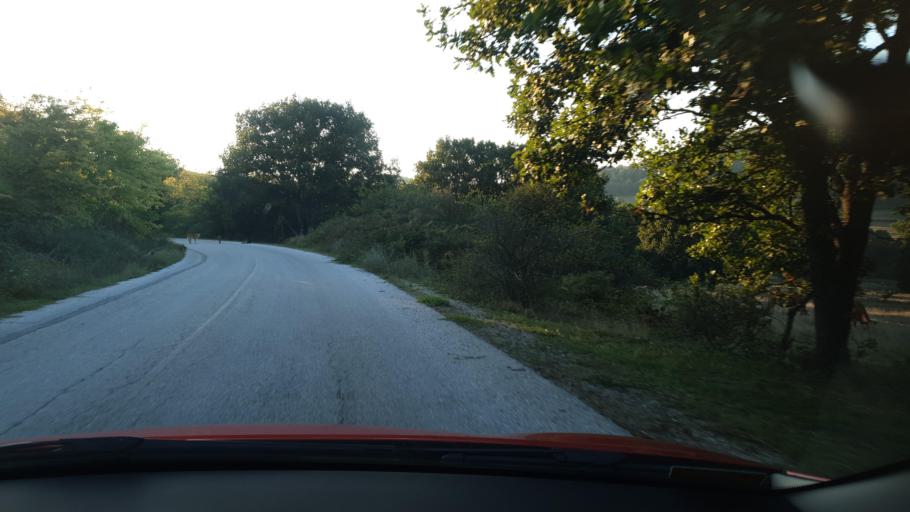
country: GR
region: Central Macedonia
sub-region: Nomos Chalkidikis
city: Galatista
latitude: 40.5035
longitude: 23.2312
